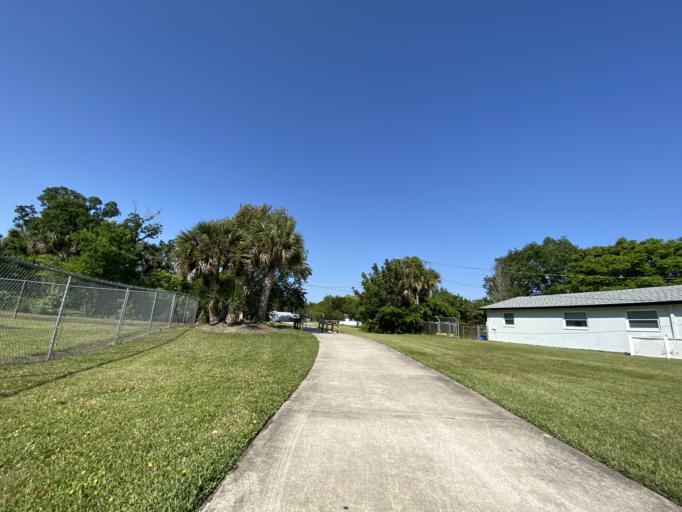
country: US
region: Florida
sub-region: Volusia County
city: South Daytona
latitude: 29.1671
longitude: -81.0107
